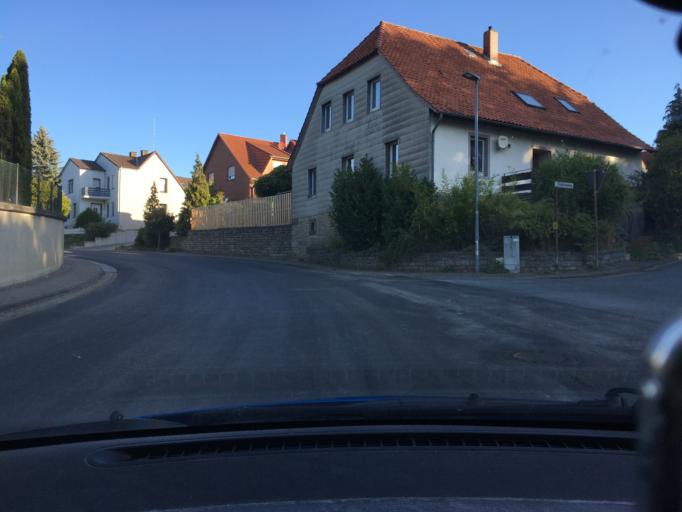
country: DE
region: Lower Saxony
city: Messenkamp
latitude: 52.2350
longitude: 9.4257
